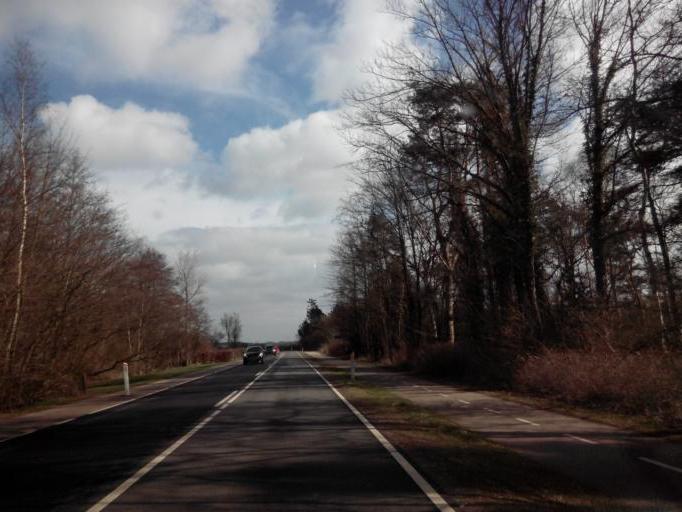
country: DK
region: Central Jutland
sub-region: Syddjurs Kommune
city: Ebeltoft
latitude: 56.2277
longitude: 10.6283
